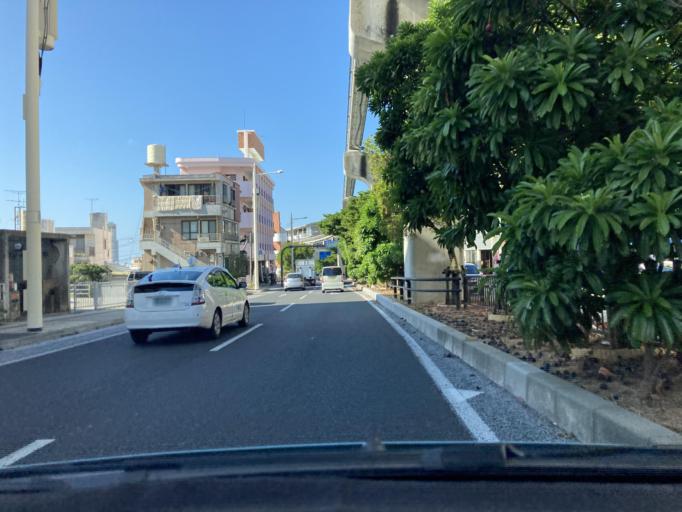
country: JP
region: Okinawa
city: Naha-shi
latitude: 26.2232
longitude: 127.7204
